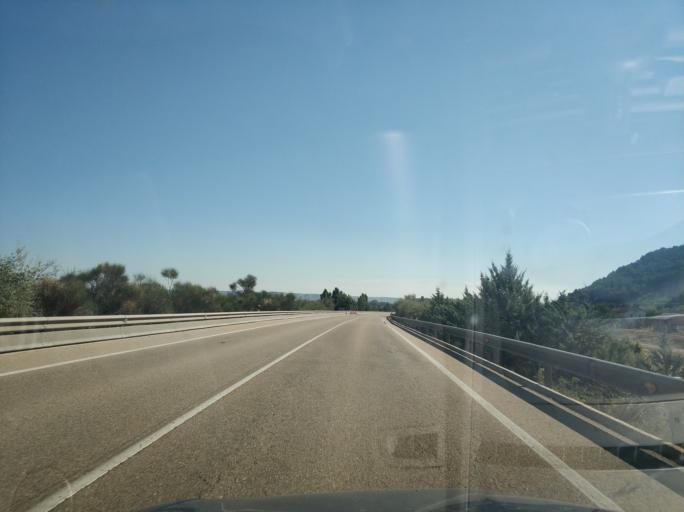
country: ES
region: Castille and Leon
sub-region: Provincia de Valladolid
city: Quintanilla de Arriba
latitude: 41.6177
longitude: -4.2116
